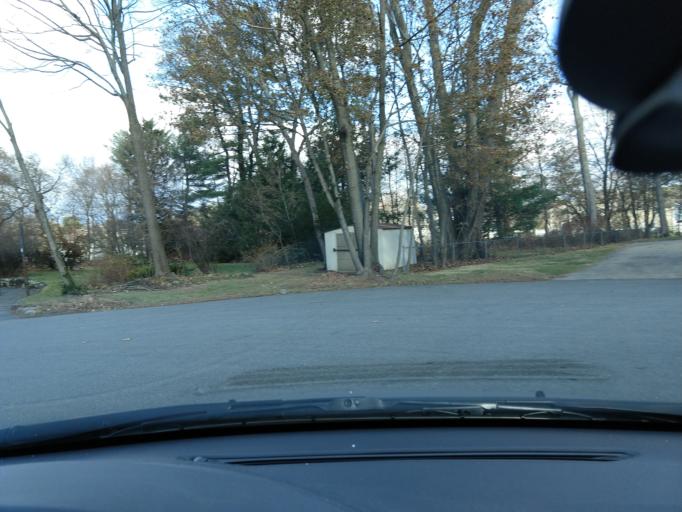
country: US
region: Massachusetts
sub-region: Middlesex County
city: Bedford
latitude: 42.4900
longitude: -71.2595
